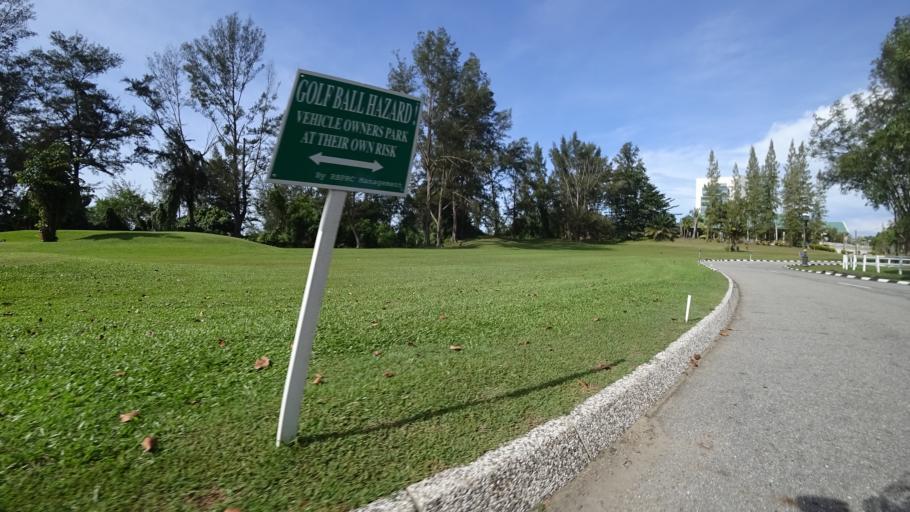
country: BN
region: Brunei and Muara
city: Bandar Seri Begawan
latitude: 4.9474
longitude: 114.8289
